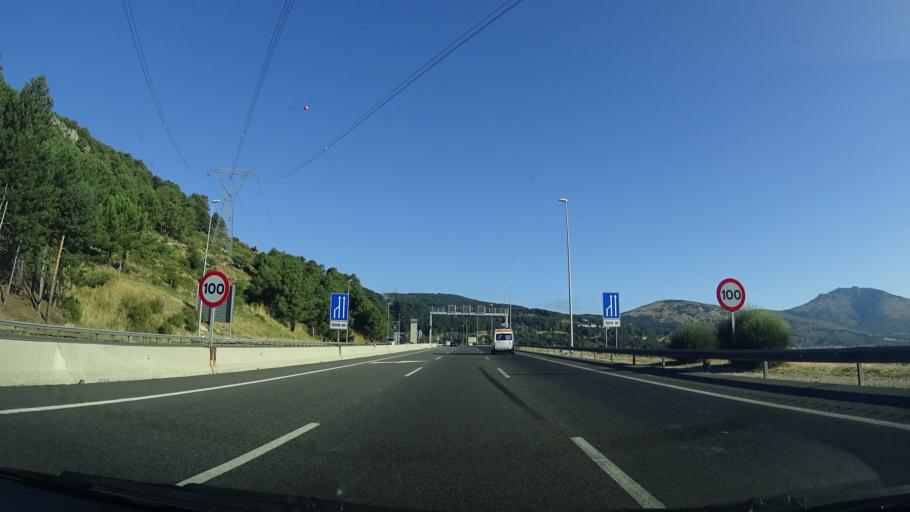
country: ES
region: Madrid
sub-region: Provincia de Madrid
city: Guadarrama
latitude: 40.6930
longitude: -4.1240
